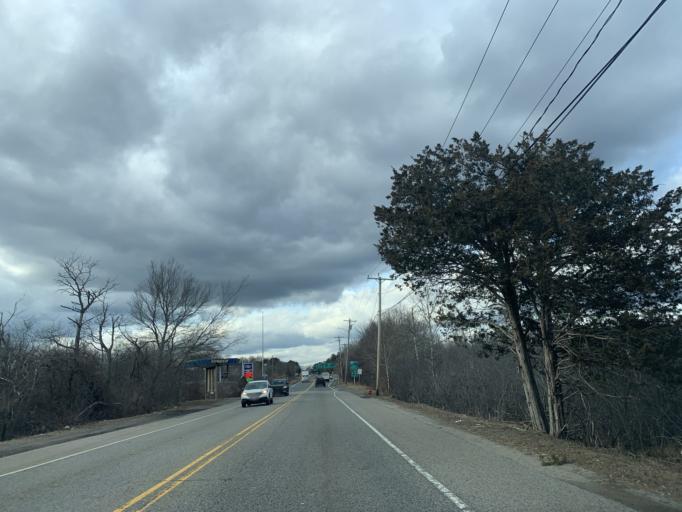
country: US
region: Massachusetts
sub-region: Norfolk County
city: Canton
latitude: 42.1671
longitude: -71.1655
